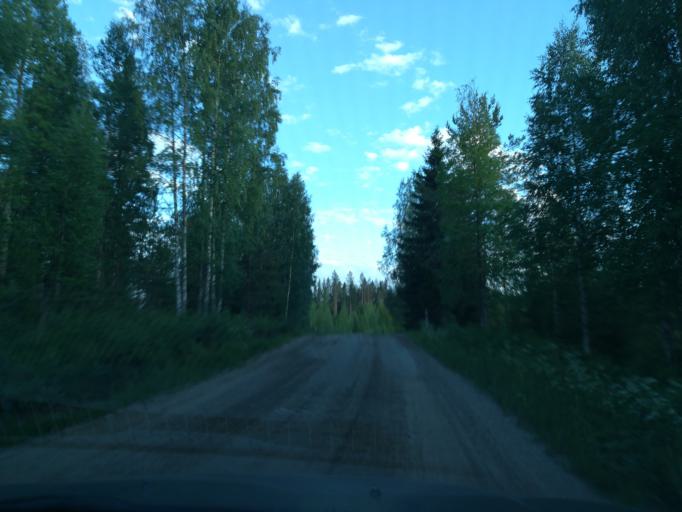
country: FI
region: Southern Savonia
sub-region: Mikkeli
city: Puumala
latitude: 61.6193
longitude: 28.1119
